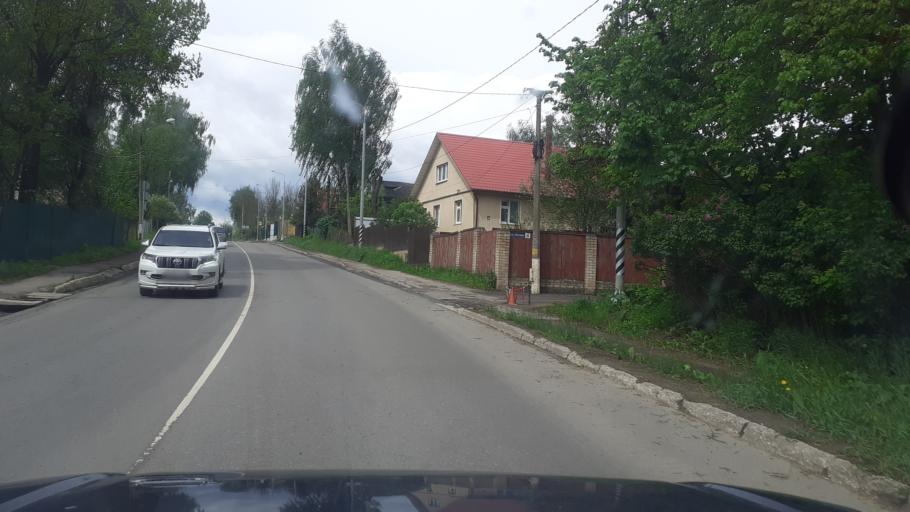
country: RU
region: Moskovskaya
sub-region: Volokolamskiy Rayon
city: Volokolamsk
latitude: 56.0416
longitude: 35.9551
